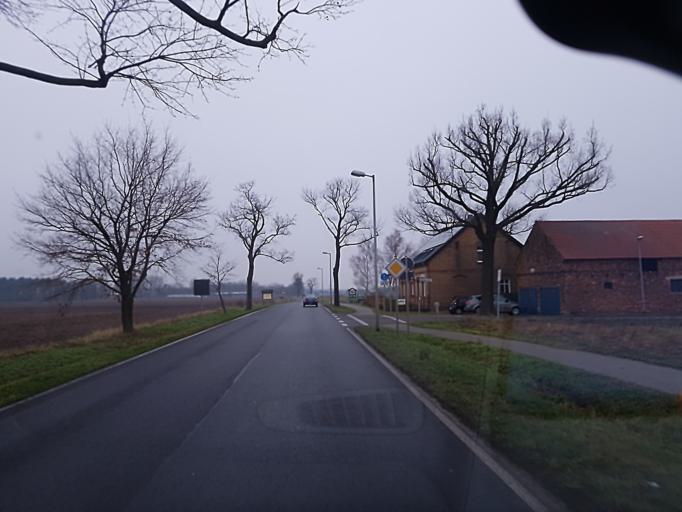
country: DE
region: Brandenburg
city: Lubbenau
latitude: 51.8704
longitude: 13.9164
